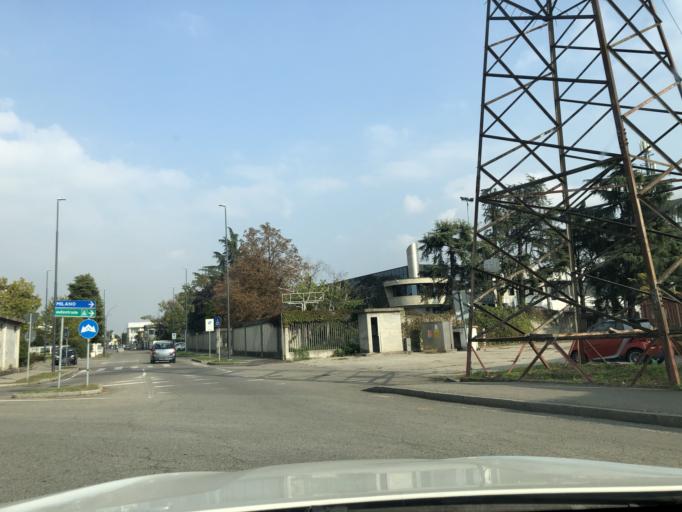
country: IT
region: Lombardy
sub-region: Citta metropolitana di Milano
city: Trezzano sul Naviglio
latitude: 45.4280
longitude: 9.0810
